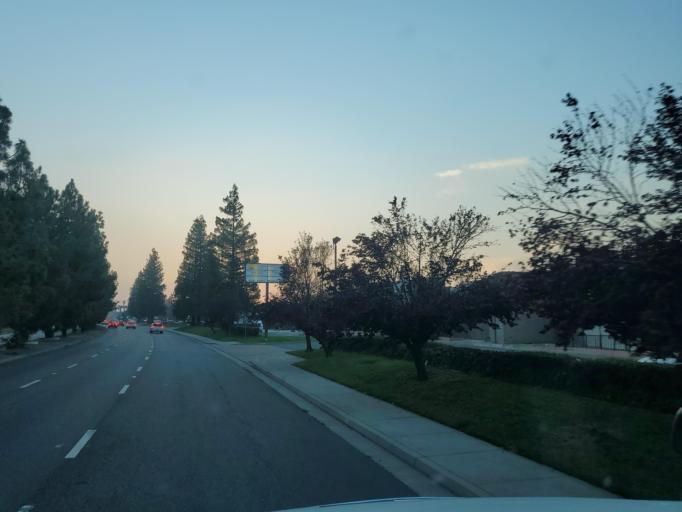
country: US
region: California
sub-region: San Joaquin County
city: Lincoln Village
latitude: 37.9995
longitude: -121.3009
